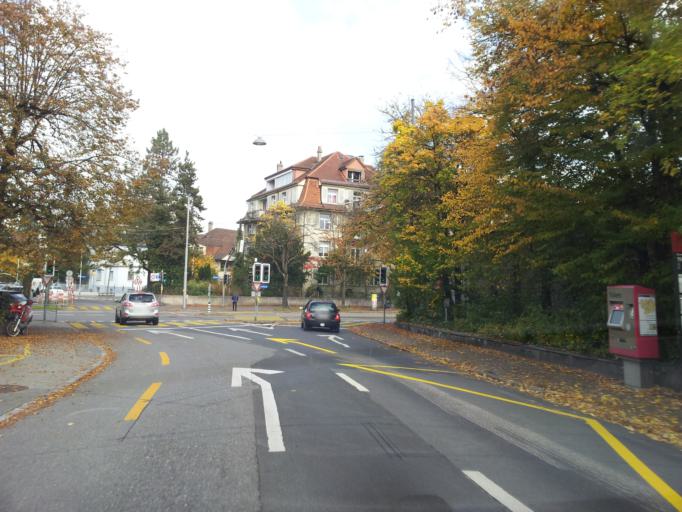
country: CH
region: Bern
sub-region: Bern-Mittelland District
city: Bern
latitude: 46.9406
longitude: 7.4632
